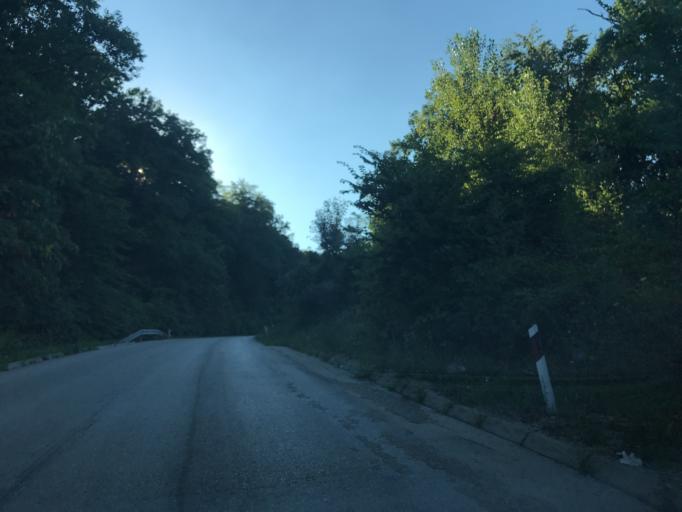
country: RS
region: Central Serbia
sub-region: Borski Okrug
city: Negotin
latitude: 44.2194
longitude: 22.4874
